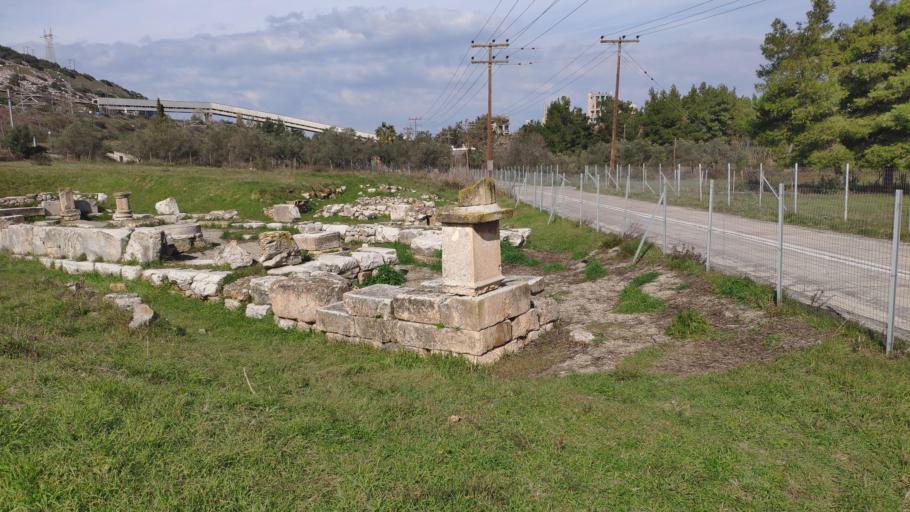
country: GR
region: Central Greece
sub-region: Nomos Evvoias
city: Chalkida
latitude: 38.4332
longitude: 23.5925
